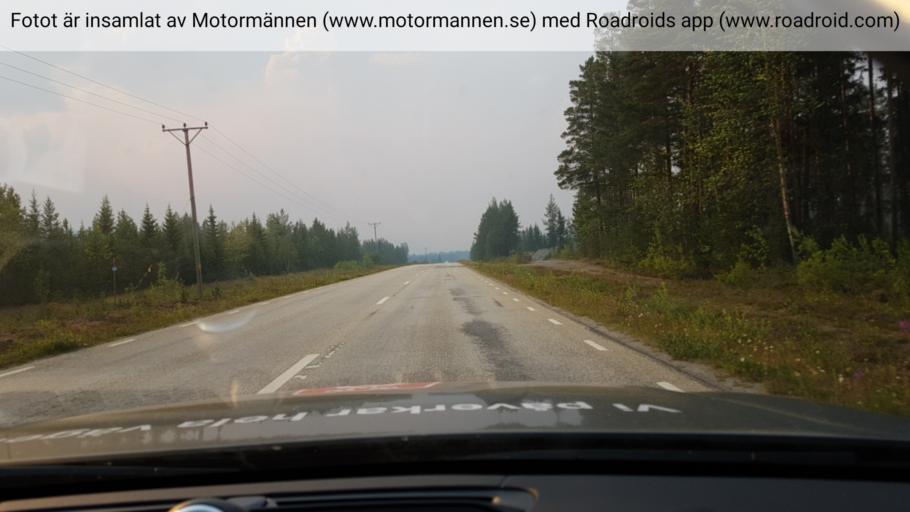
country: SE
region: Jaemtland
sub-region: Bergs Kommun
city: Hoverberg
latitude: 62.4936
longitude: 14.2162
